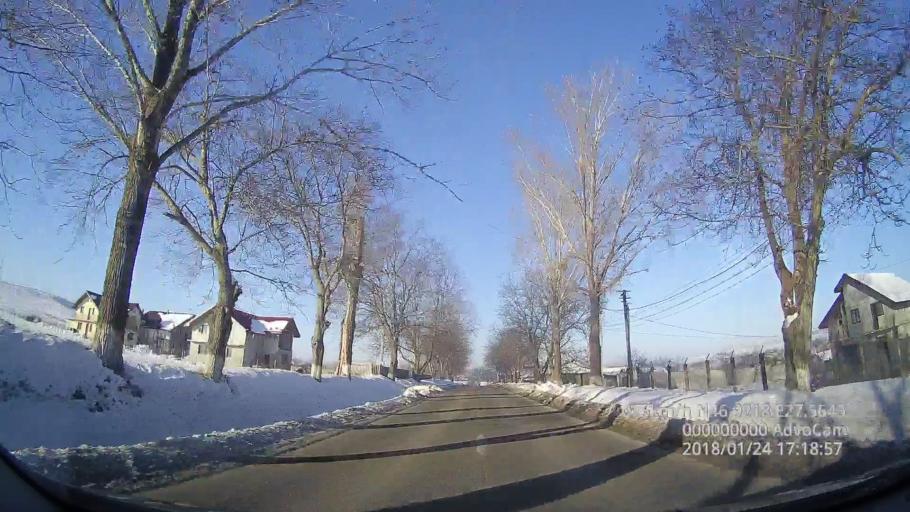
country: RO
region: Iasi
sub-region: Comuna Scanteia
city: Scanteia
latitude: 46.9224
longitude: 27.5643
